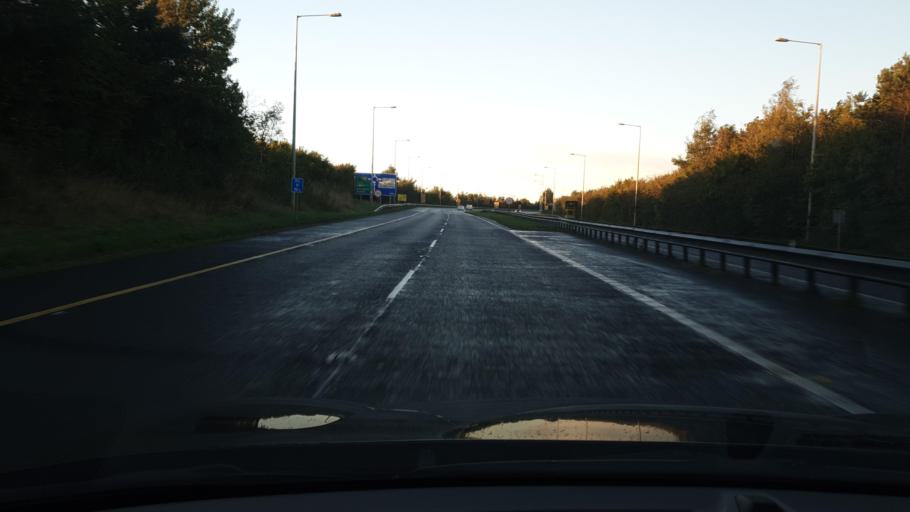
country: IE
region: Leinster
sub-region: An Mhi
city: Ashbourne
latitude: 53.5211
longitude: -6.4193
